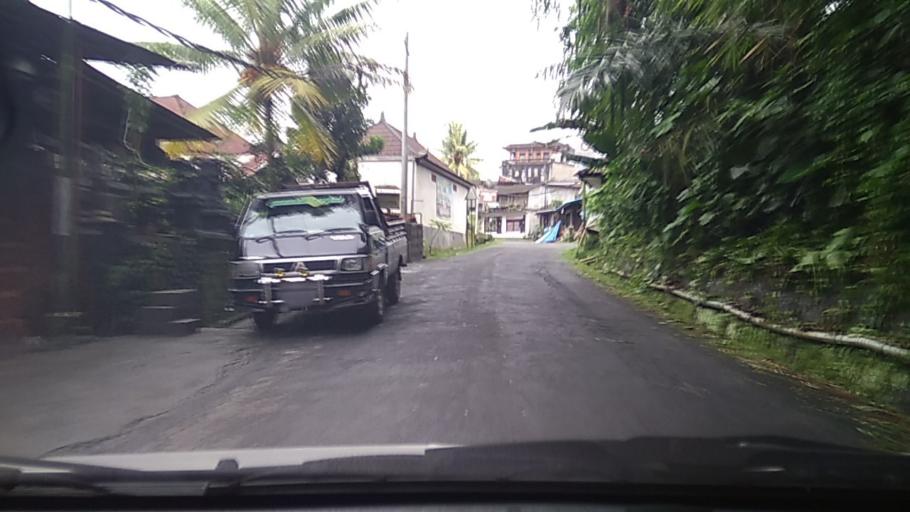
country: ID
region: Bali
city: Banjar Dujung Kaja
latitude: -8.4051
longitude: 115.2912
